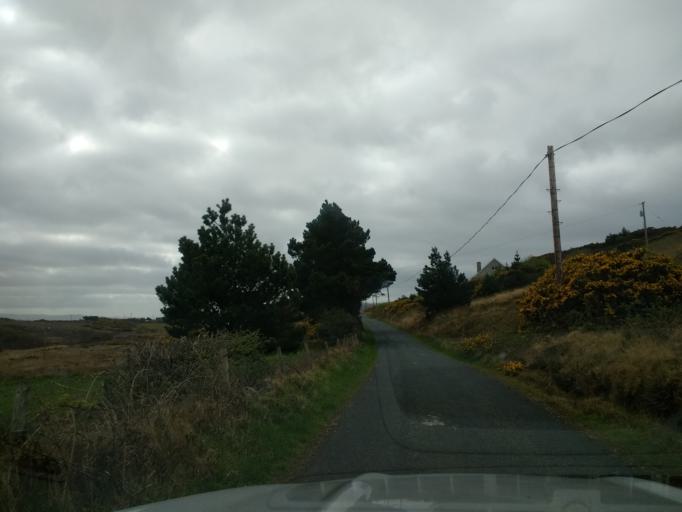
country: IE
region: Ulster
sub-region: County Donegal
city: Ramelton
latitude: 55.2600
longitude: -7.6368
